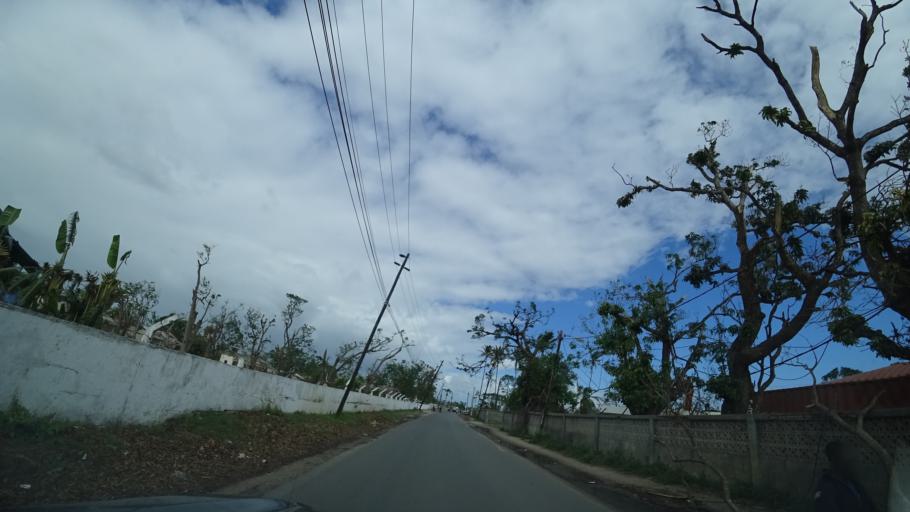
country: MZ
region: Sofala
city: Beira
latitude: -19.8045
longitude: 34.9046
